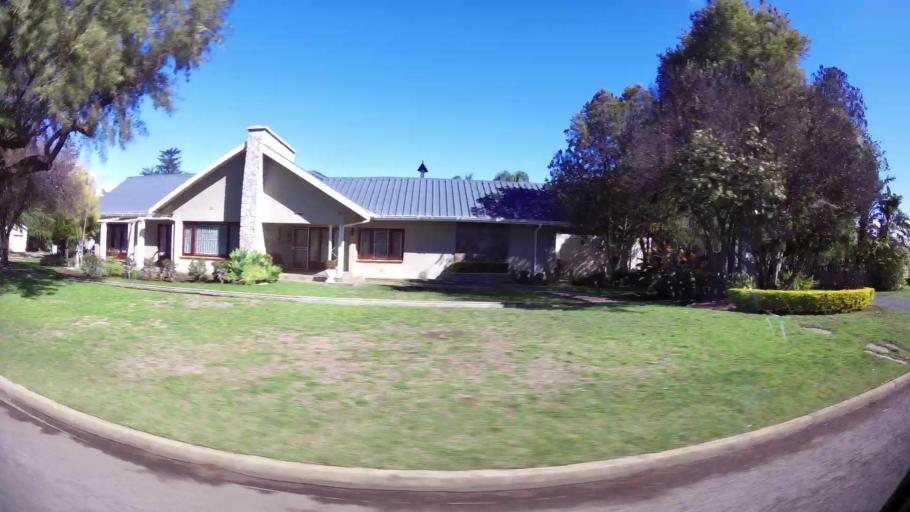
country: ZA
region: Western Cape
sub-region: Cape Winelands District Municipality
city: Ashton
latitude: -33.8064
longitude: 19.8944
